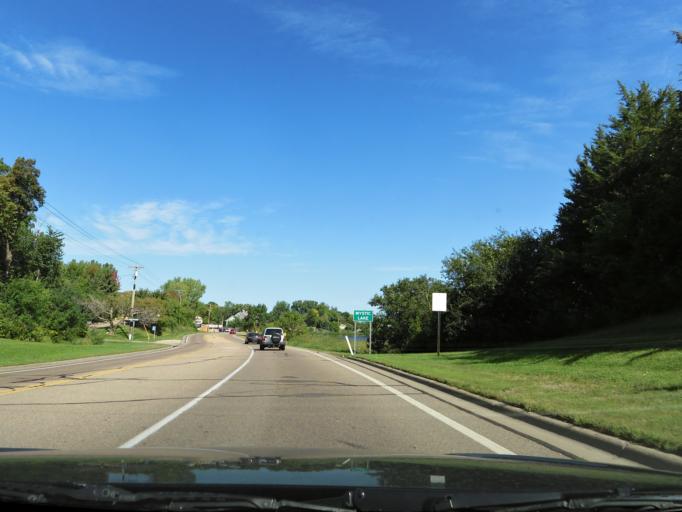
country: US
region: Minnesota
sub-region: Scott County
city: Prior Lake
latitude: 44.7351
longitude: -93.4698
